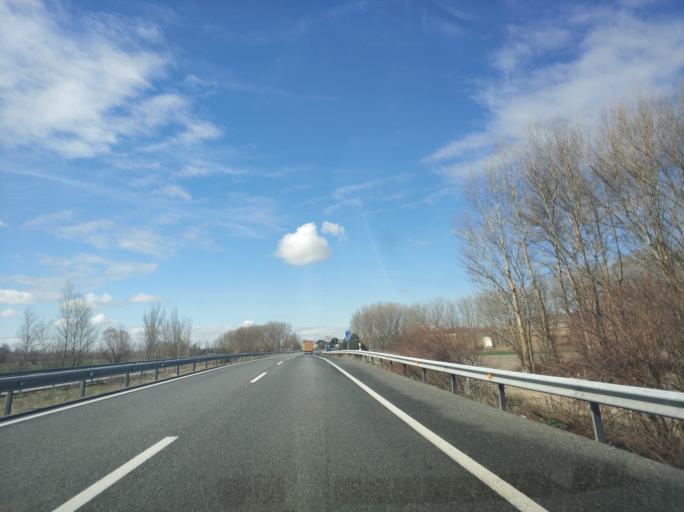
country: ES
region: Castille and Leon
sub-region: Provincia de Burgos
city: Celada del Camino
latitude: 42.2680
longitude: -3.9218
